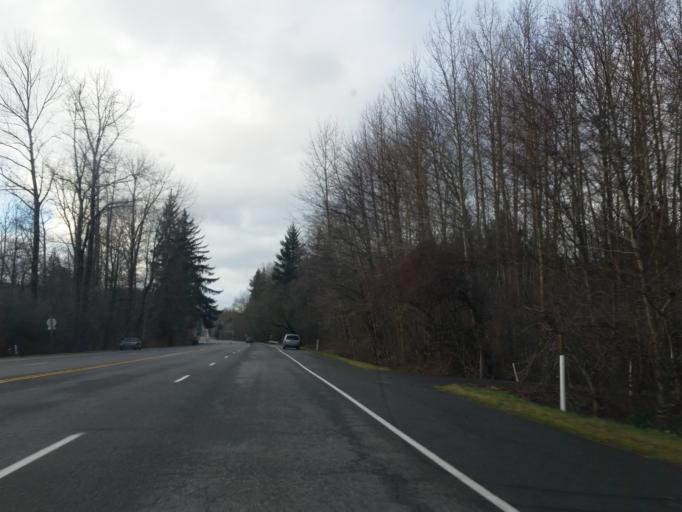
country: US
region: Washington
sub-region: King County
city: North Bend
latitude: 47.5028
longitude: -121.8022
